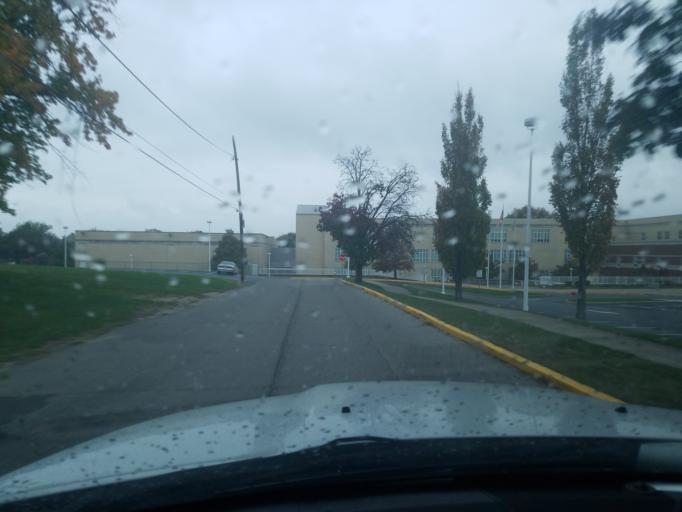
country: US
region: Indiana
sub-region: Floyd County
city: New Albany
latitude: 38.2982
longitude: -85.8098
